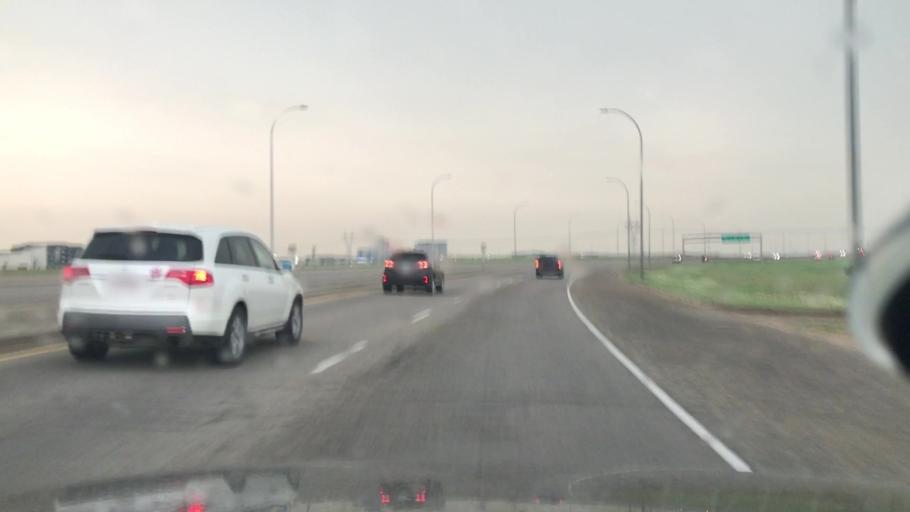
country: CA
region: Alberta
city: Edmonton
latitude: 53.4483
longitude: -113.5915
